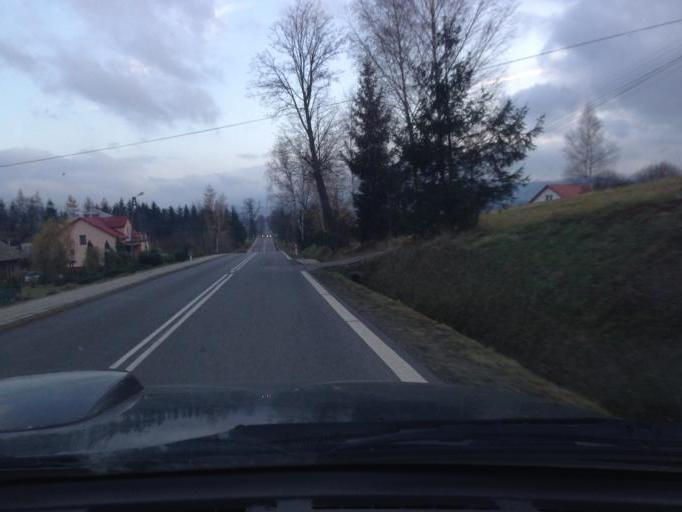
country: PL
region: Subcarpathian Voivodeship
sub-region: Powiat jasielski
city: Nowy Zmigrod
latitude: 49.6378
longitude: 21.5232
